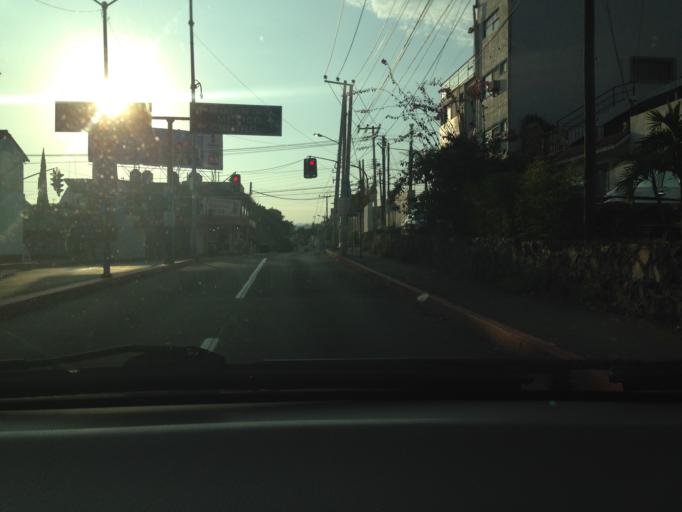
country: MX
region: Morelos
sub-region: Cuernavaca
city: Fraccionamiento Lomas de Ahuatlan
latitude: 18.9555
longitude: -99.2416
